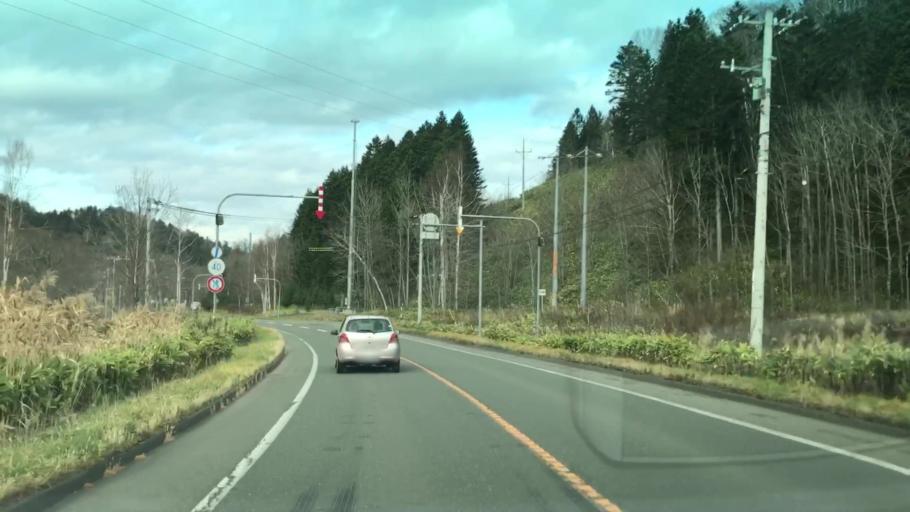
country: JP
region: Hokkaido
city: Shimo-furano
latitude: 42.9259
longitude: 142.4451
